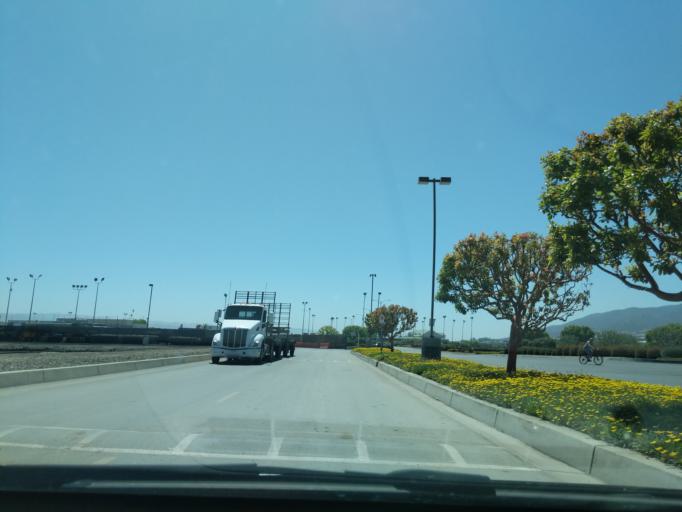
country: US
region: California
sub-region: Monterey County
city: Salinas
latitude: 36.6196
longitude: -121.6471
